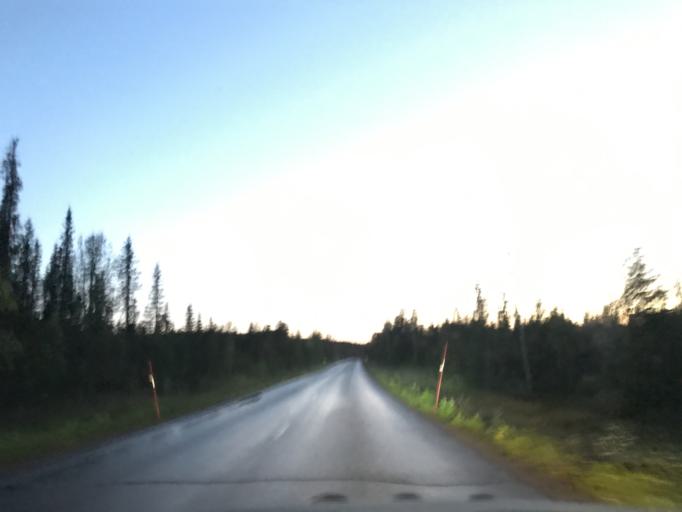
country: SE
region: Norrbotten
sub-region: Gallivare Kommun
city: Malmberget
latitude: 67.6509
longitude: 21.0311
